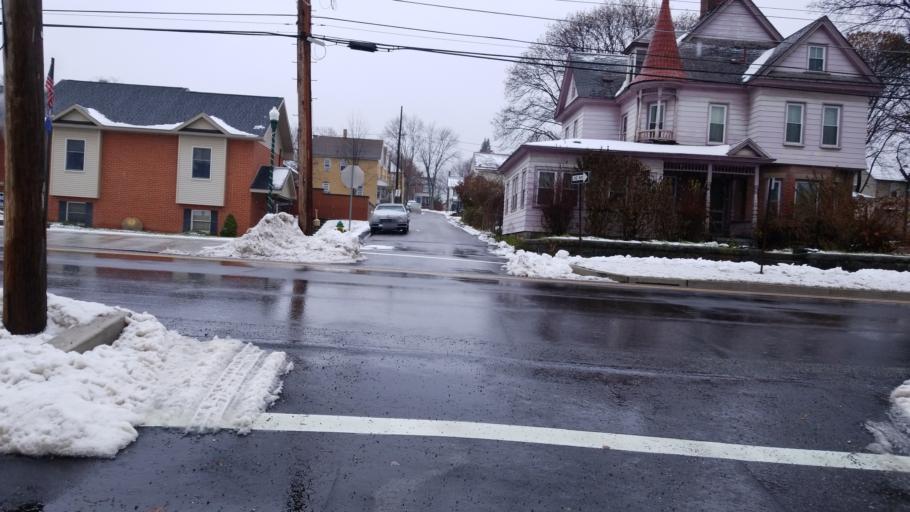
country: US
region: Pennsylvania
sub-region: Clearfield County
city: DuBois
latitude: 41.1210
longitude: -78.7675
